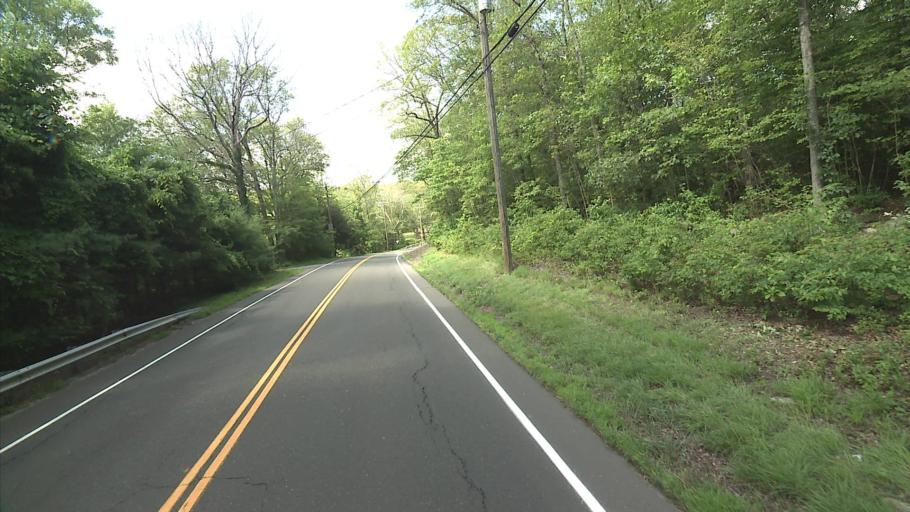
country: US
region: Connecticut
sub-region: Middlesex County
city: Higganum
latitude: 41.4039
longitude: -72.5623
